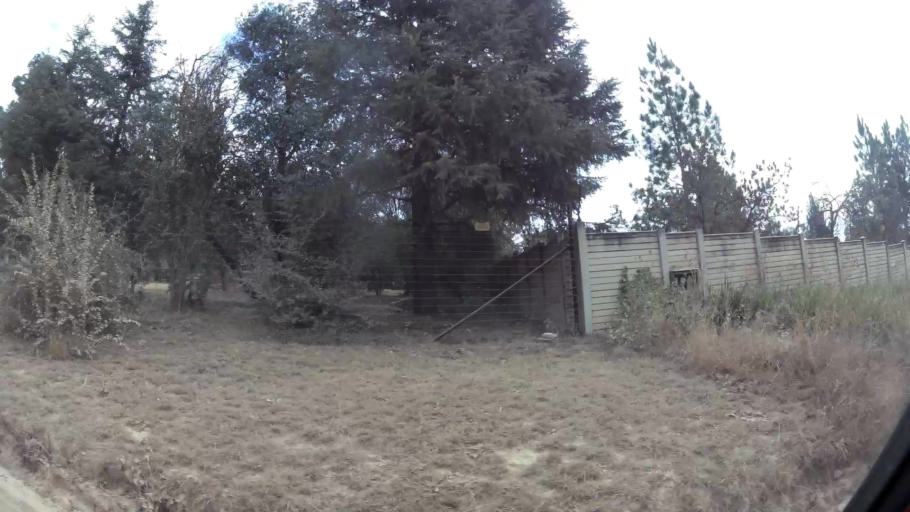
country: ZA
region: Gauteng
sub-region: West Rand District Municipality
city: Muldersdriseloop
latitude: -26.0716
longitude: 27.8796
